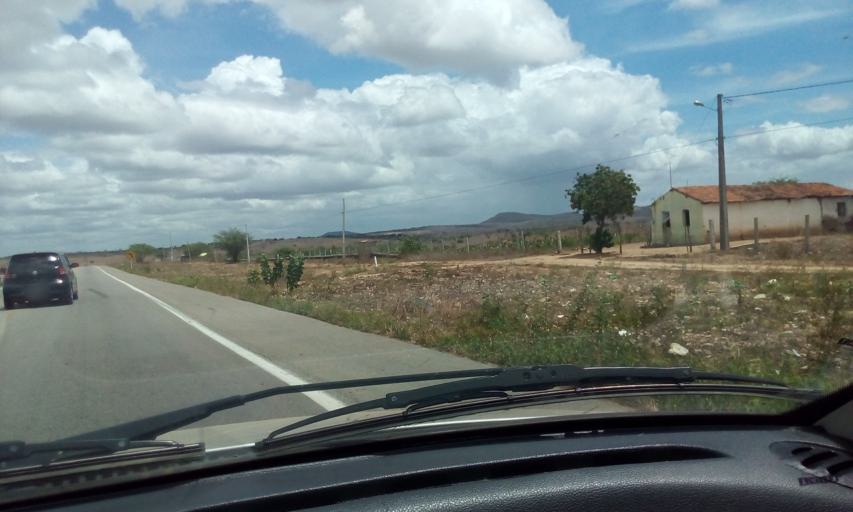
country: BR
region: Rio Grande do Norte
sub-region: Tangara
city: Tangara
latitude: -6.1893
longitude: -35.7846
